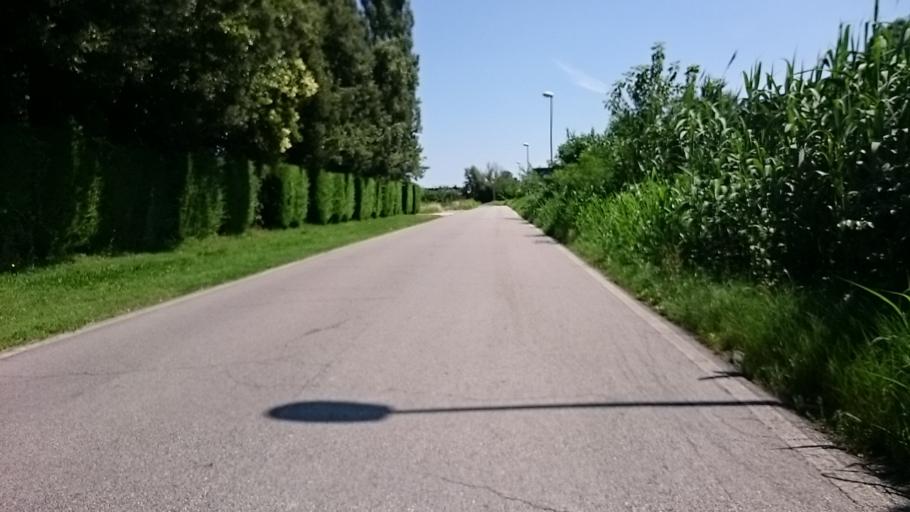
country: IT
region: Veneto
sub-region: Provincia di Padova
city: San Vito
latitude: 45.4165
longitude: 11.9582
